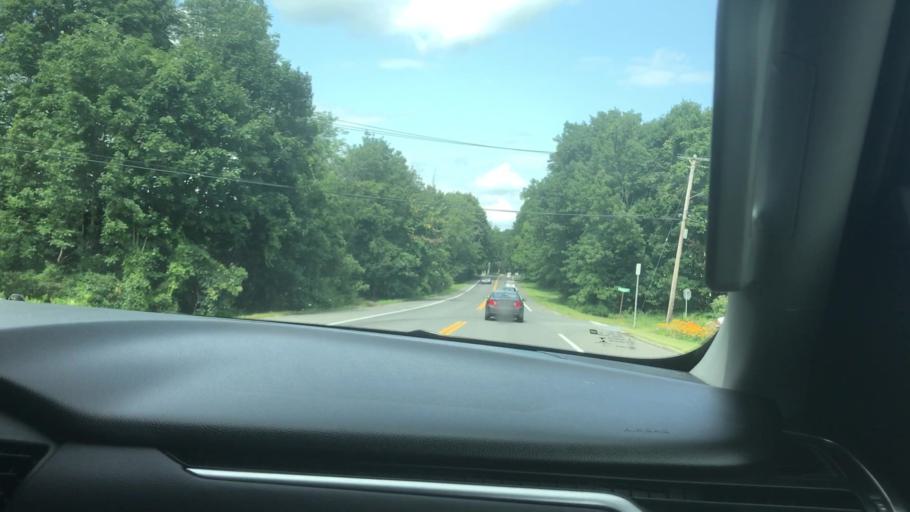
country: US
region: New York
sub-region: Dutchess County
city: Dover Plains
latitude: 41.8594
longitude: -73.5525
